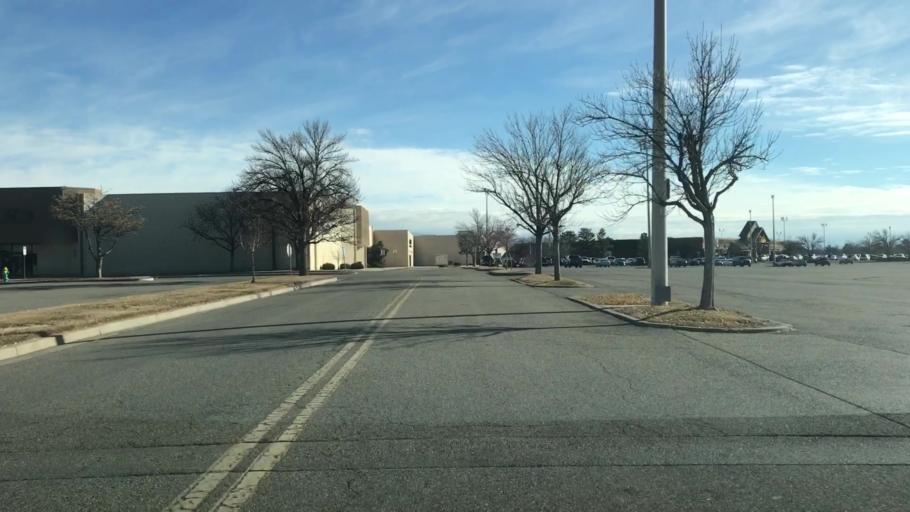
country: US
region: Colorado
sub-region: Mesa County
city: Redlands
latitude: 39.0922
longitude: -108.6060
